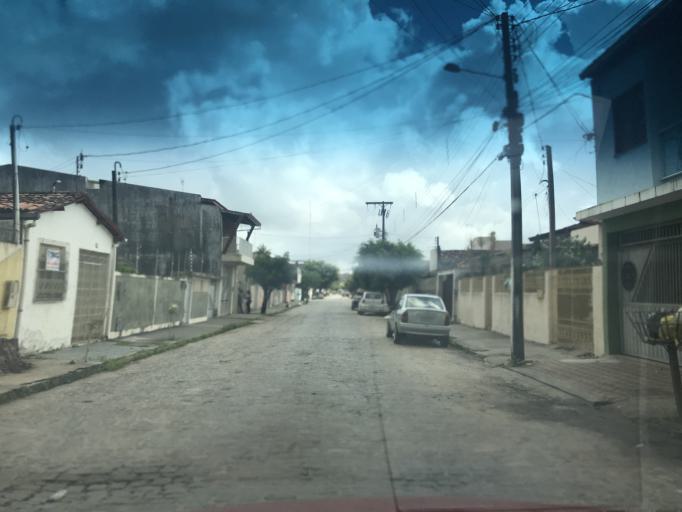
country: BR
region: Bahia
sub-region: Cruz Das Almas
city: Cruz das Almas
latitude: -12.6760
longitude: -39.0989
